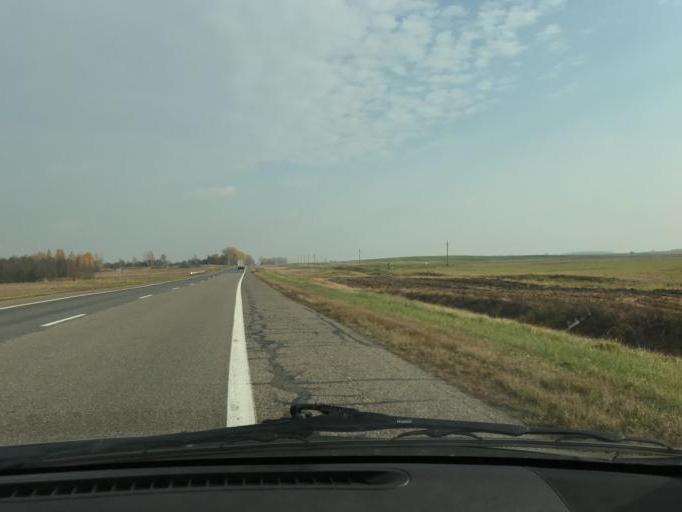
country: BY
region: Vitebsk
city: Chashniki
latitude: 55.0059
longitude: 28.9716
